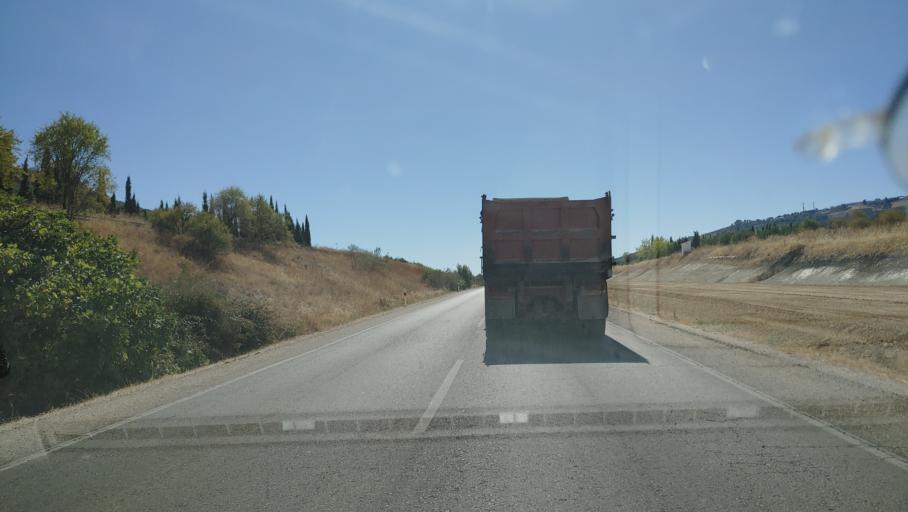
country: ES
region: Andalusia
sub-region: Provincia de Jaen
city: Villanueva del Arzobispo
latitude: 38.1583
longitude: -2.9993
